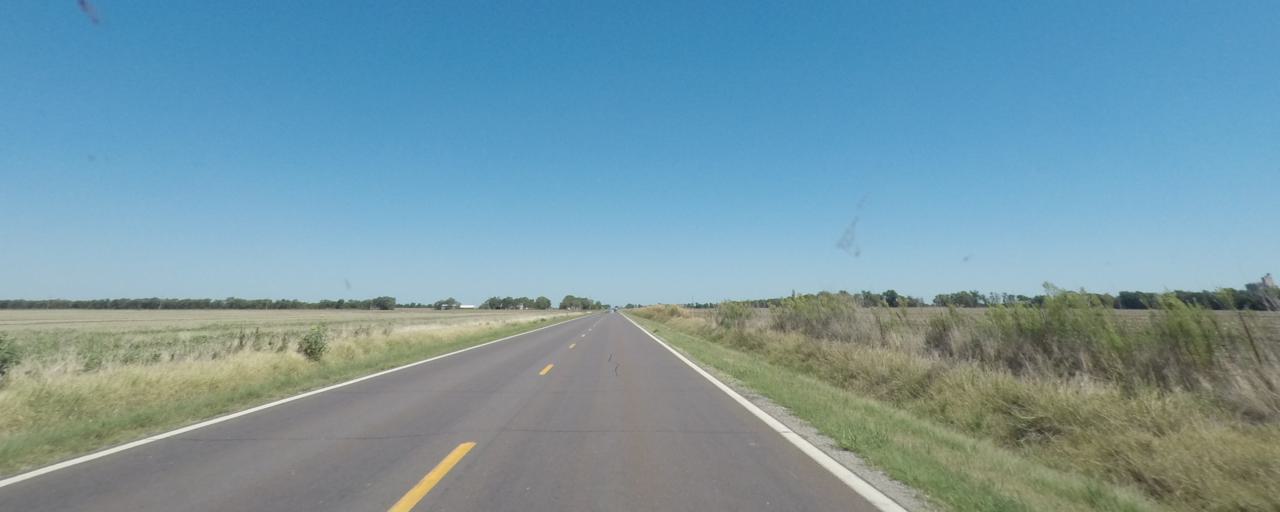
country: US
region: Kansas
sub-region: Sumner County
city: Wellington
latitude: 37.1519
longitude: -97.4023
